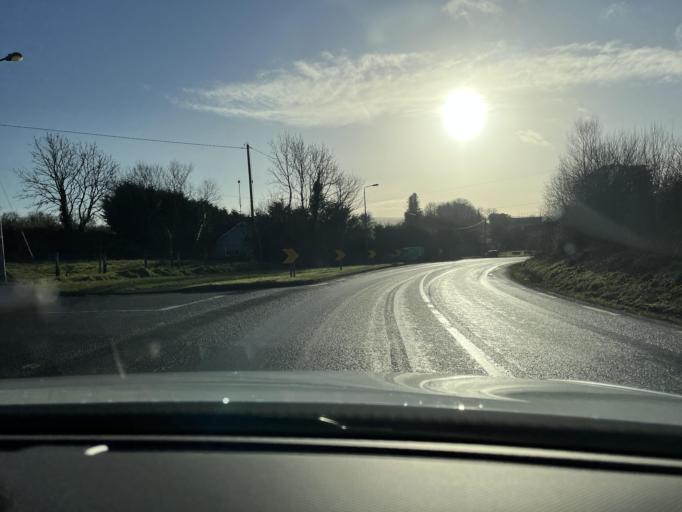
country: IE
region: Connaught
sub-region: County Leitrim
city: Manorhamilton
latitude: 54.2329
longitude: -8.2071
